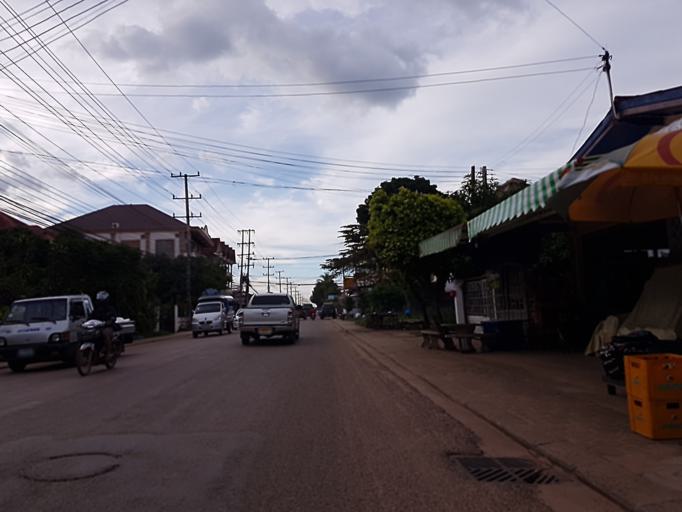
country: LA
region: Vientiane
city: Vientiane
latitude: 17.9825
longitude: 102.5833
